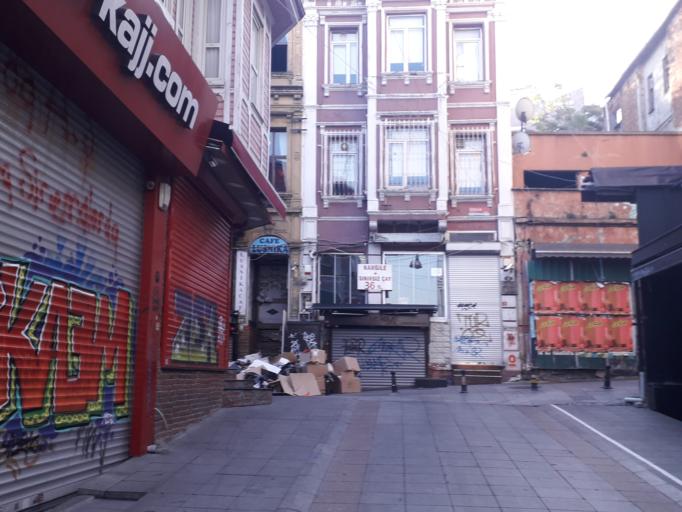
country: TR
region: Istanbul
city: UEskuedar
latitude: 40.9903
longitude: 29.0255
